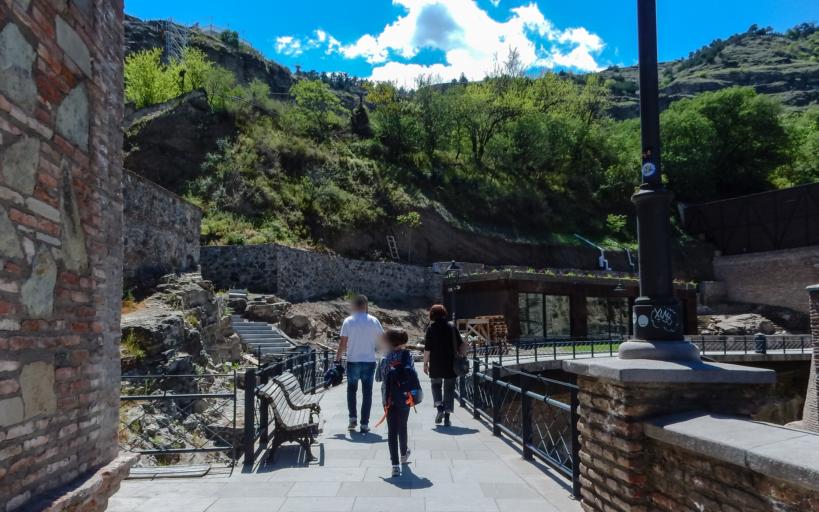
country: GE
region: T'bilisi
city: Tbilisi
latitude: 41.6874
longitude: 44.8111
